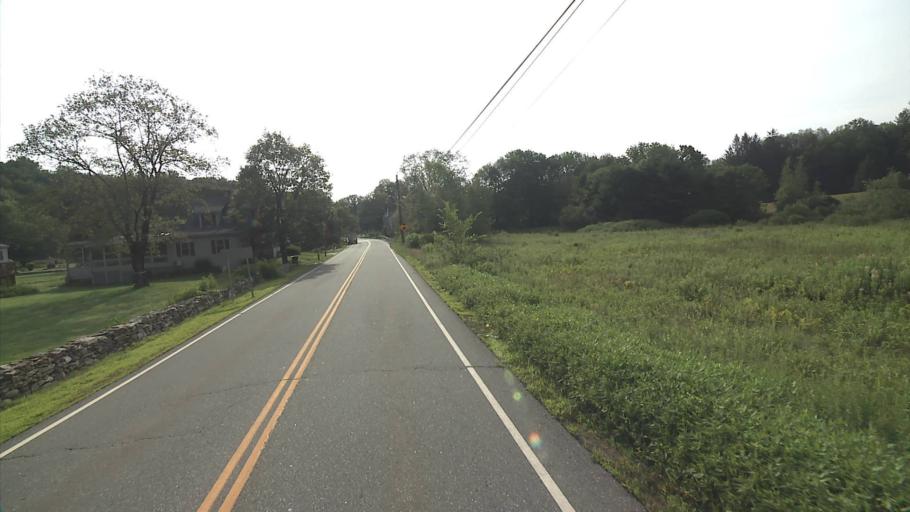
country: US
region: Connecticut
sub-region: Windham County
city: Quinebaug
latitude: 41.9922
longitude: -71.9997
